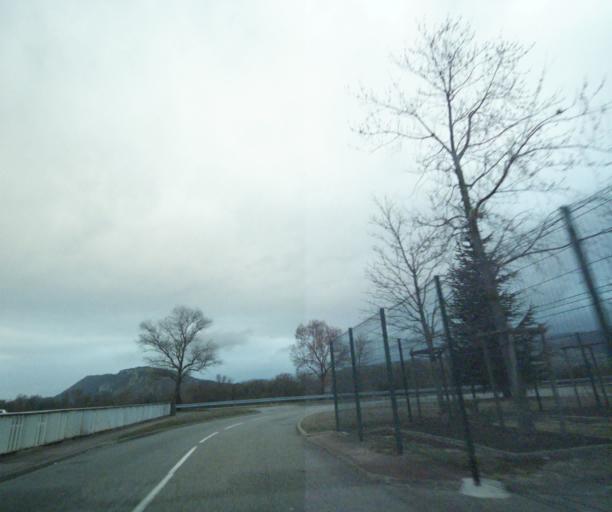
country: FR
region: Rhone-Alpes
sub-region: Departement de l'Ardeche
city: Cornas
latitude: 44.9603
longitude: 4.8713
